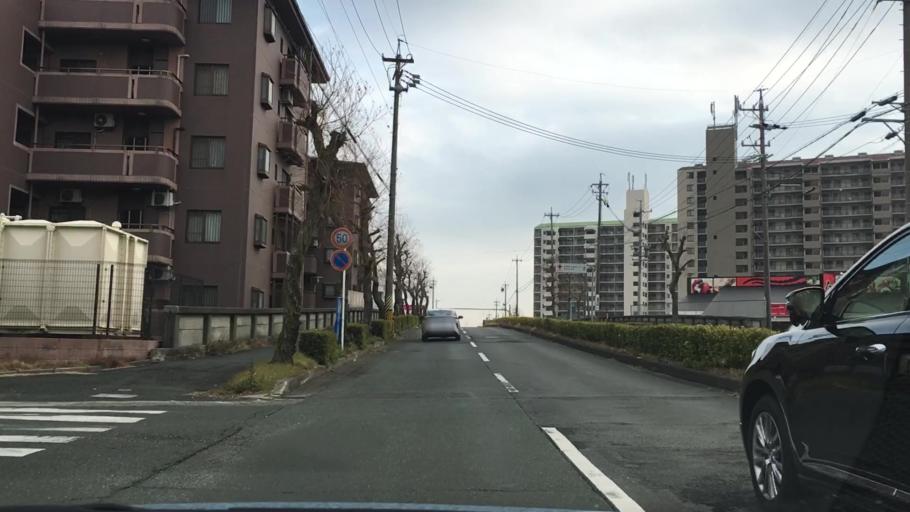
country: JP
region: Aichi
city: Toyohashi
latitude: 34.7537
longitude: 137.3731
